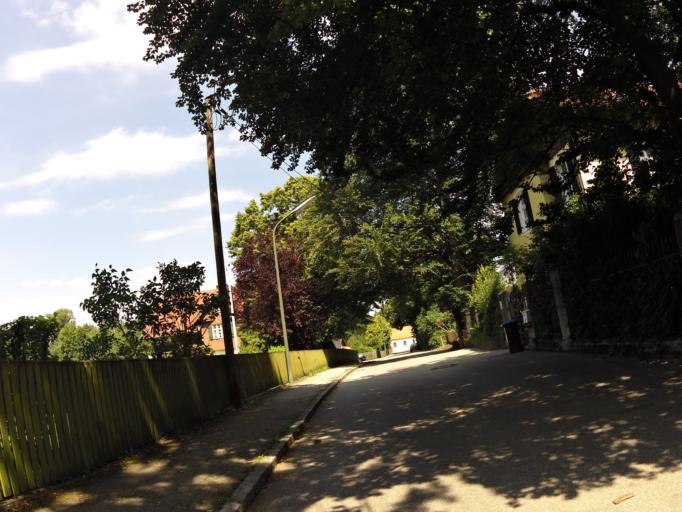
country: DE
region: Bavaria
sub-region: Upper Bavaria
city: Inning am Ammersee
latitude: 48.0549
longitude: 11.1364
